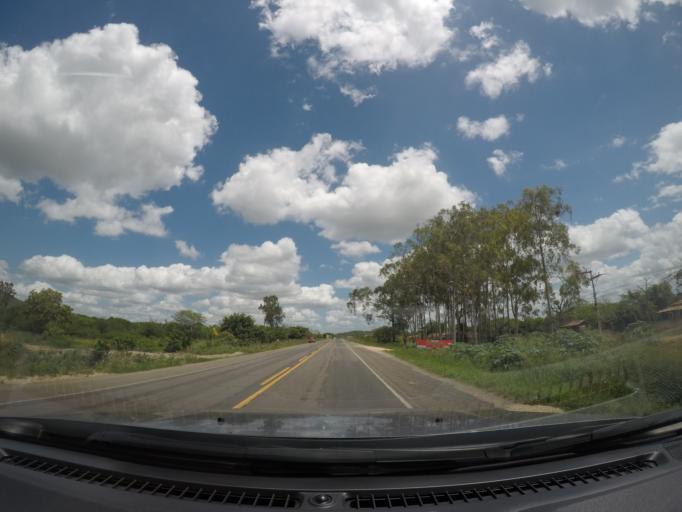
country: BR
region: Bahia
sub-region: Ipira
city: Ipira
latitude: -12.1958
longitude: -39.6931
